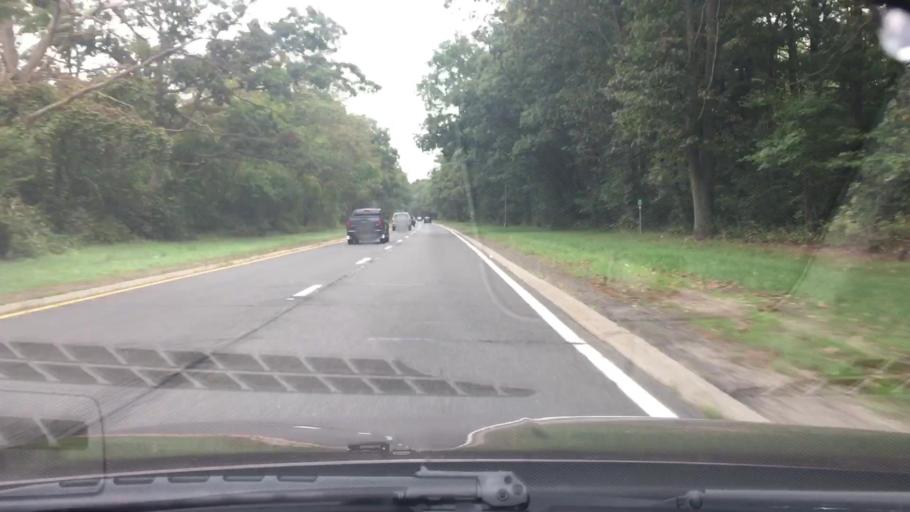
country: US
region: New York
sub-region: Suffolk County
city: South Huntington
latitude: 40.8006
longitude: -73.3915
